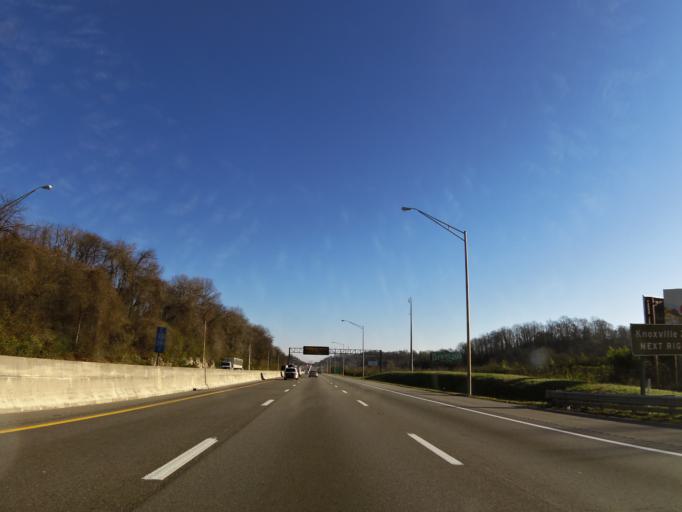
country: US
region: Tennessee
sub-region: Knox County
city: Knoxville
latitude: 36.0031
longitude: -83.8836
